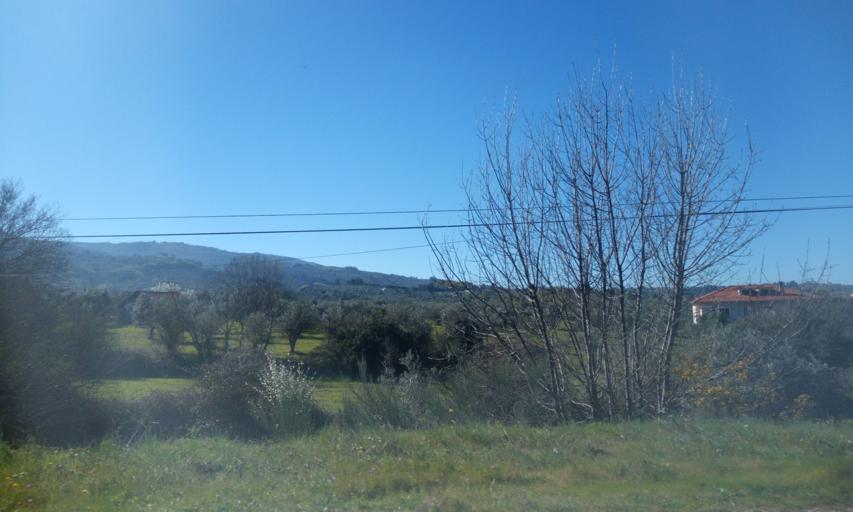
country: PT
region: Guarda
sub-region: Fornos de Algodres
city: Fornos de Algodres
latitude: 40.5295
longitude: -7.5585
